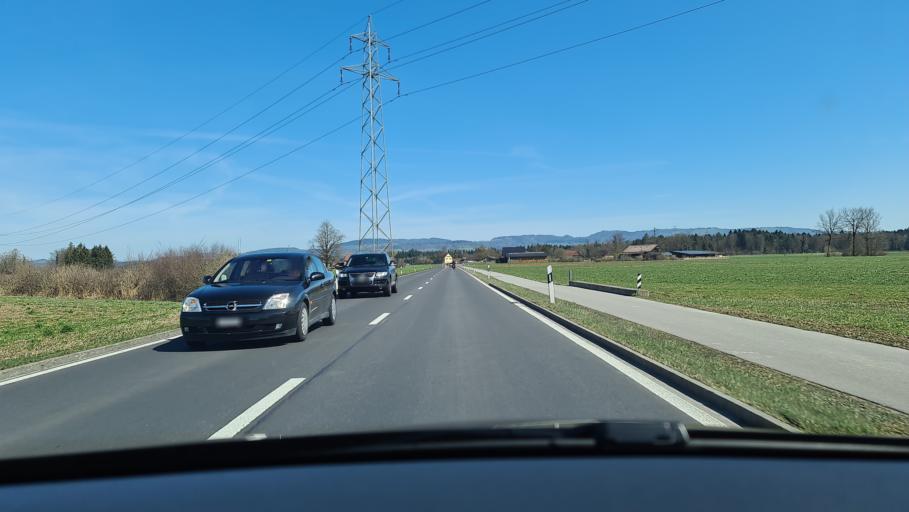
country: CH
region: Aargau
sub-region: Bezirk Muri
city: Sins
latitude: 47.1888
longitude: 8.4046
